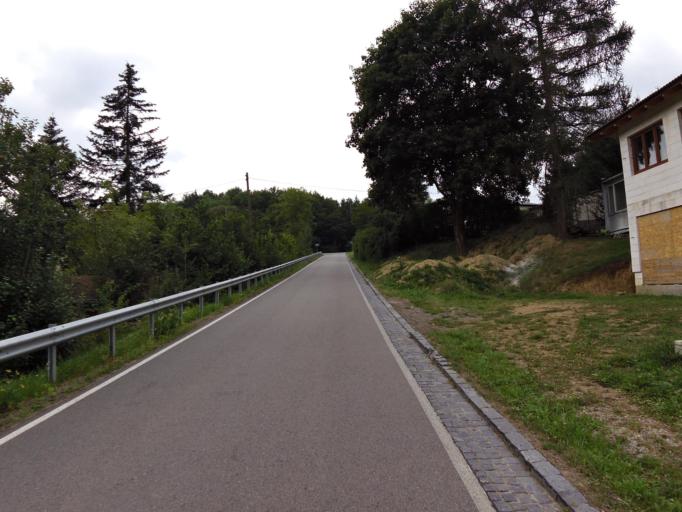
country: CZ
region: Central Bohemia
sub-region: Okres Benesov
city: Pysely
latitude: 49.8661
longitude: 14.6597
